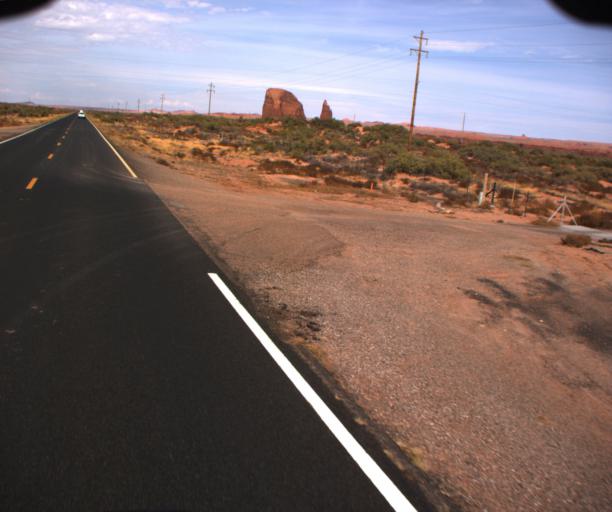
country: US
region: Arizona
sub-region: Apache County
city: Many Farms
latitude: 36.6399
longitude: -109.5883
